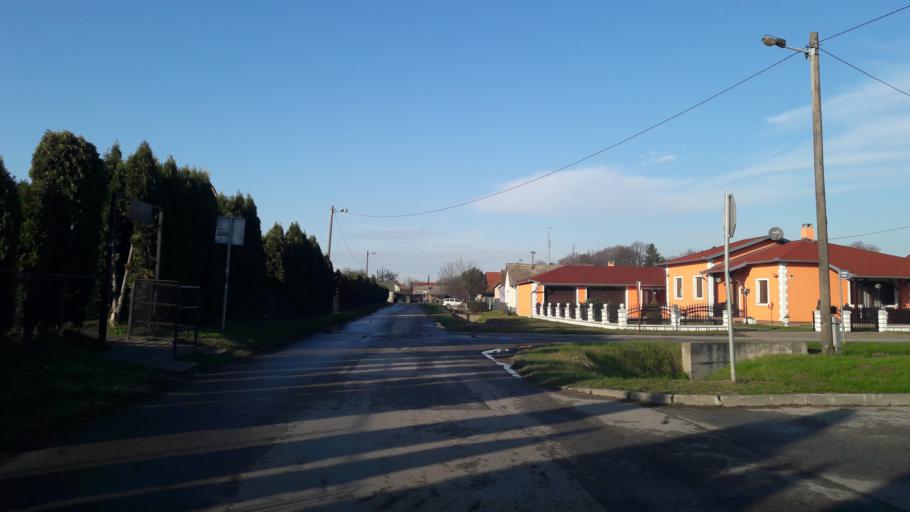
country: HR
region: Osjecko-Baranjska
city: Darda
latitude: 45.6261
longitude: 18.6992
